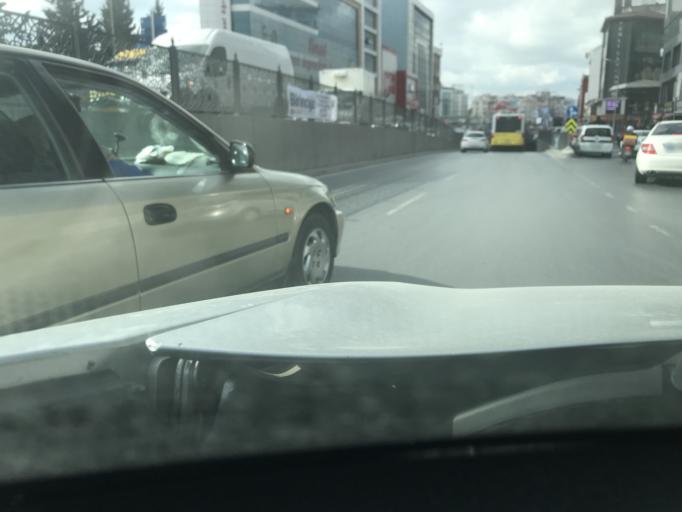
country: TR
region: Istanbul
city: Esenyurt
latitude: 41.0323
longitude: 28.6816
